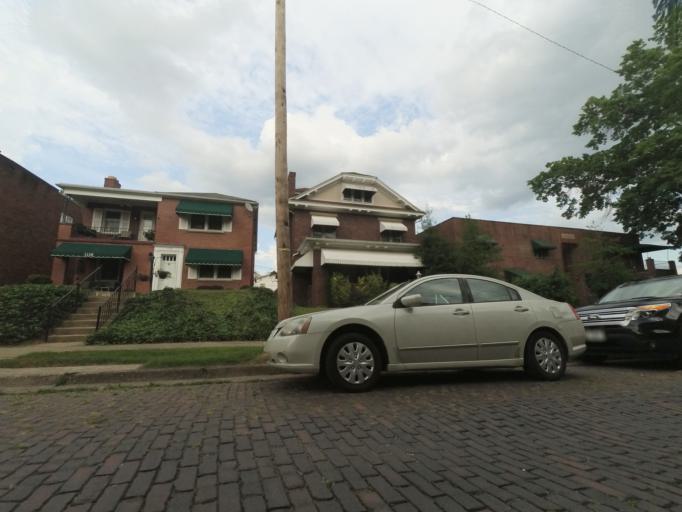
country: US
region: West Virginia
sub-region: Cabell County
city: Huntington
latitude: 38.4120
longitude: -82.4342
